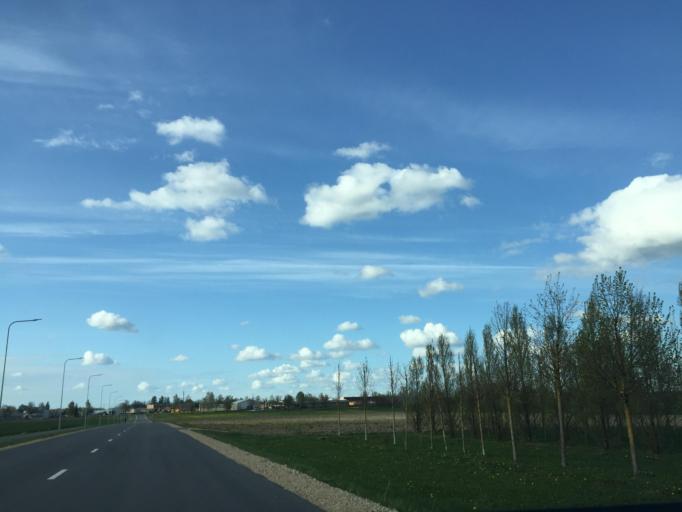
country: LV
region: Sigulda
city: Sigulda
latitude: 57.1361
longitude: 24.8618
